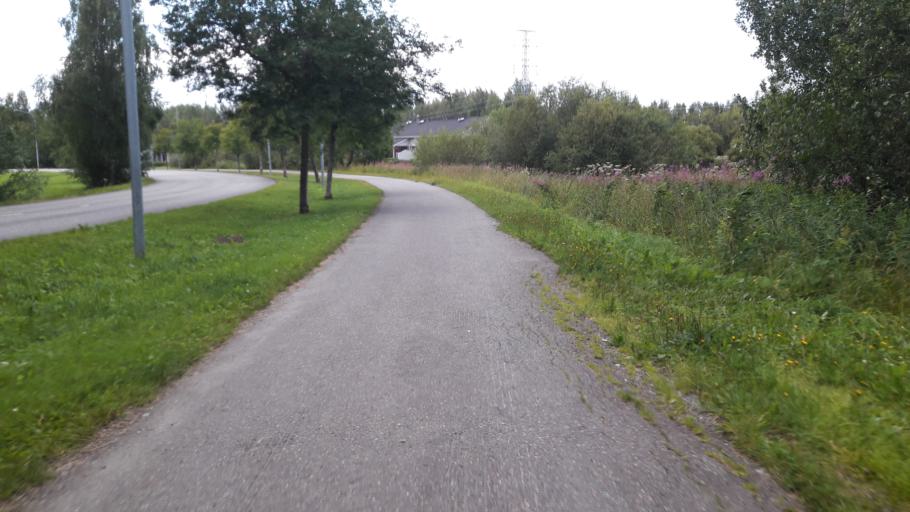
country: FI
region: North Karelia
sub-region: Joensuu
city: Joensuu
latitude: 62.5906
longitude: 29.8056
